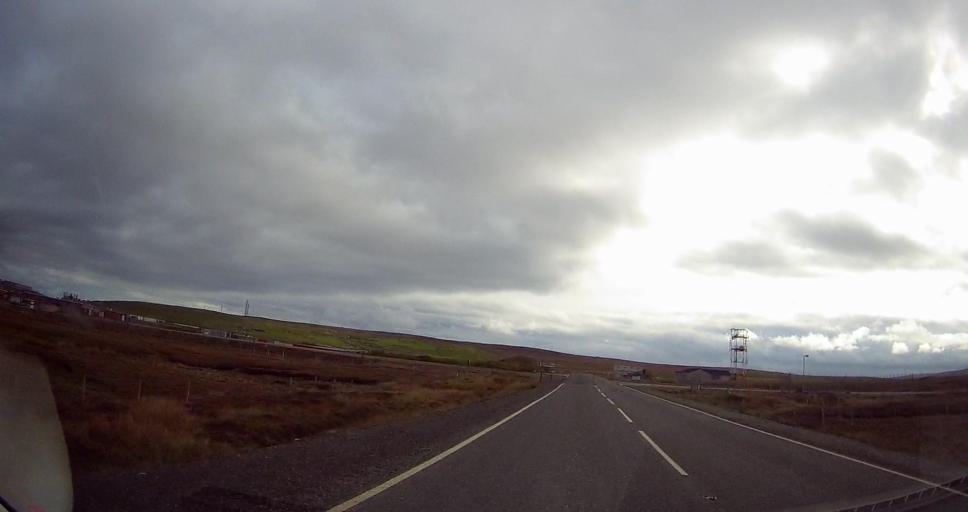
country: GB
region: Scotland
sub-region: Shetland Islands
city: Lerwick
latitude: 60.4388
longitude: -1.2754
